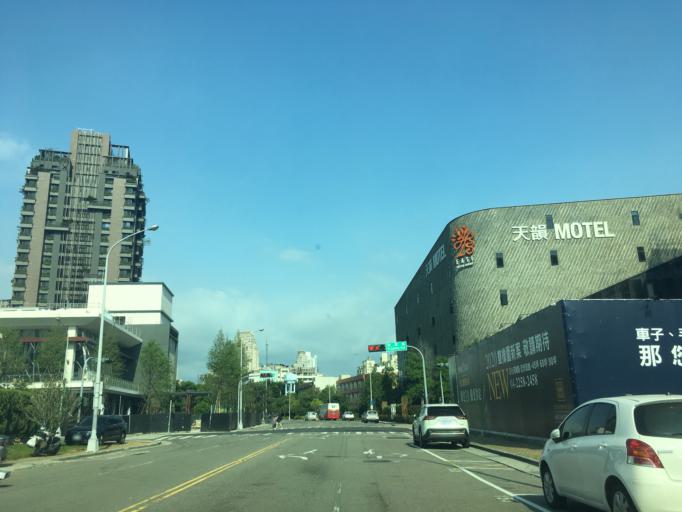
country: TW
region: Taiwan
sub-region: Taichung City
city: Taichung
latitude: 24.1586
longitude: 120.6304
